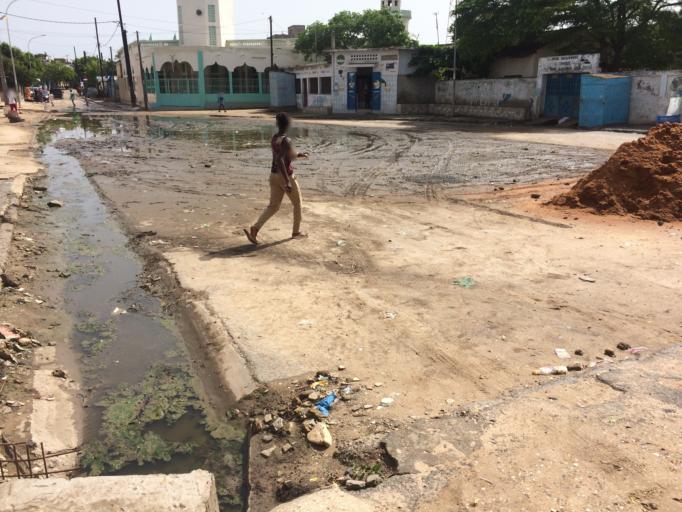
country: SN
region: Dakar
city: Pikine
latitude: 14.7289
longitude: -17.3241
